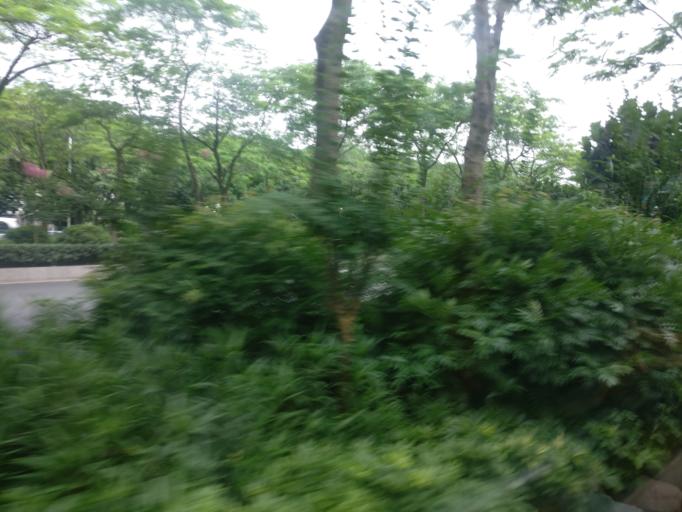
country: CN
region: Guangdong
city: Xinshi
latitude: 23.1825
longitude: 113.2732
